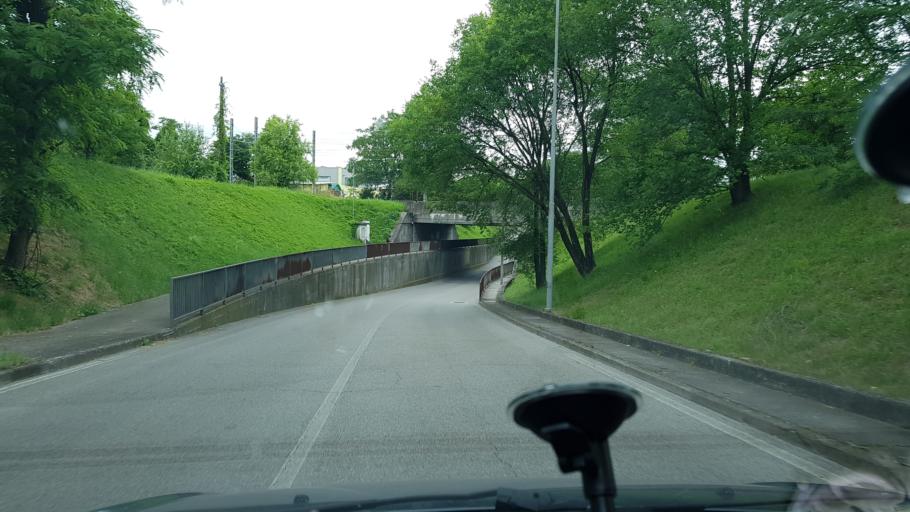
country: IT
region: Friuli Venezia Giulia
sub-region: Provincia di Gorizia
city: Gorizia
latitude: 45.9204
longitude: 13.6110
